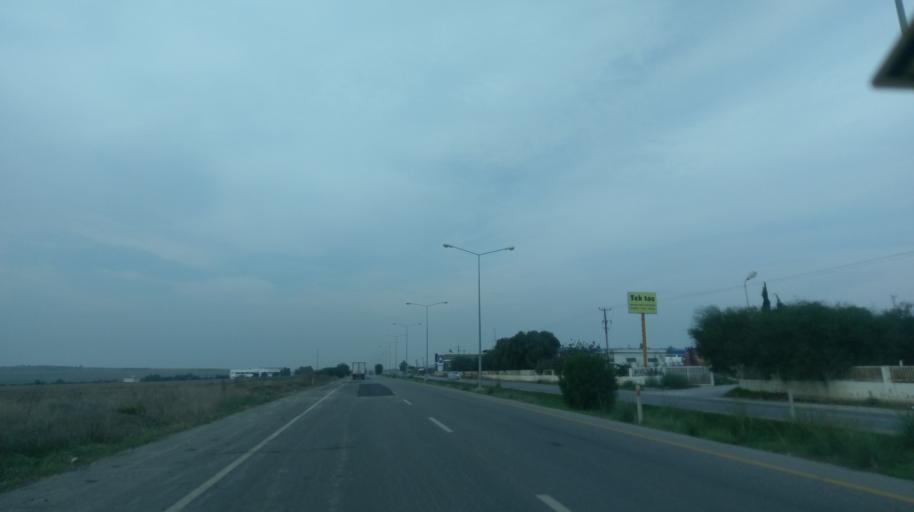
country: CY
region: Lefkosia
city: Mammari
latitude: 35.2123
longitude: 33.2581
